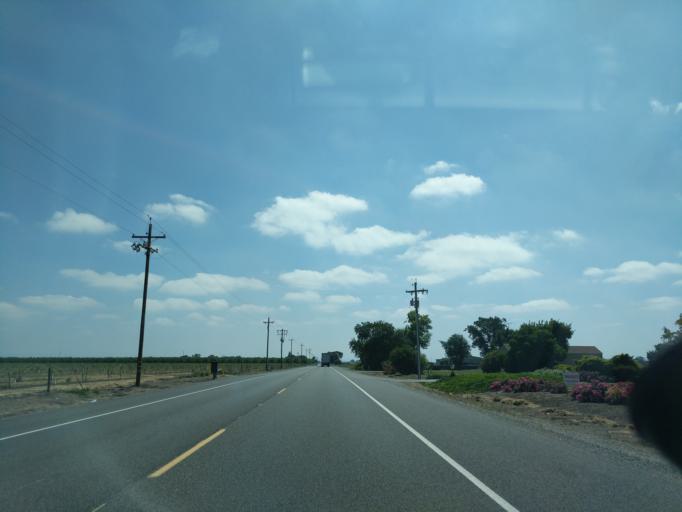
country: US
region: California
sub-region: San Joaquin County
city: Garden Acres
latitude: 37.9423
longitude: -121.1372
